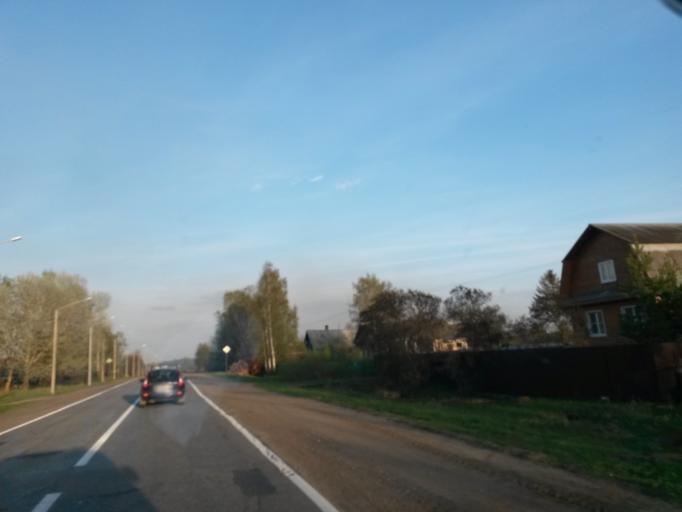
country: RU
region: Jaroslavl
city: Kurba
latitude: 57.6779
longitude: 39.5817
